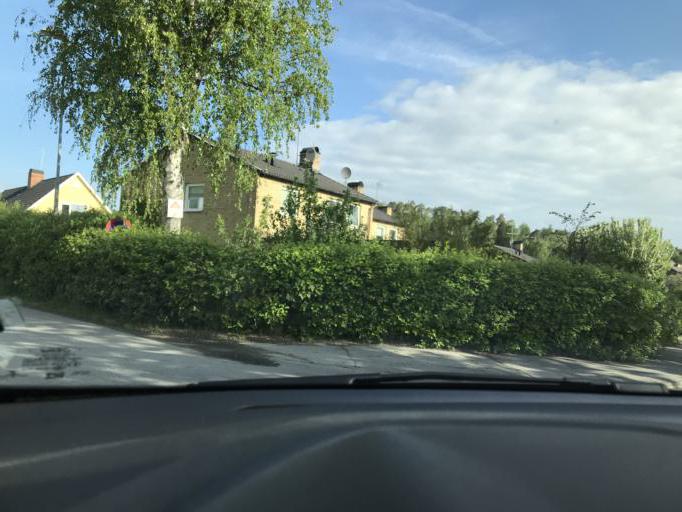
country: SE
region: Stockholm
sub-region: Botkyrka Kommun
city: Tumba
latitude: 59.1896
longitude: 17.8174
